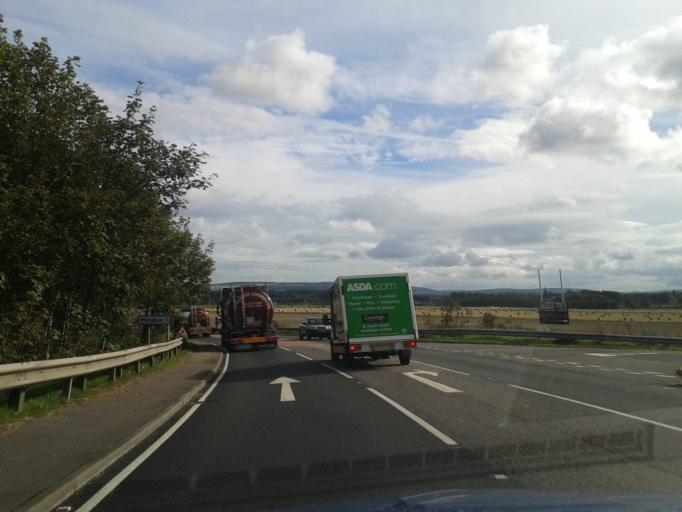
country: GB
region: Scotland
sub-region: Moray
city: Forres
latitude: 57.6018
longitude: -3.6533
